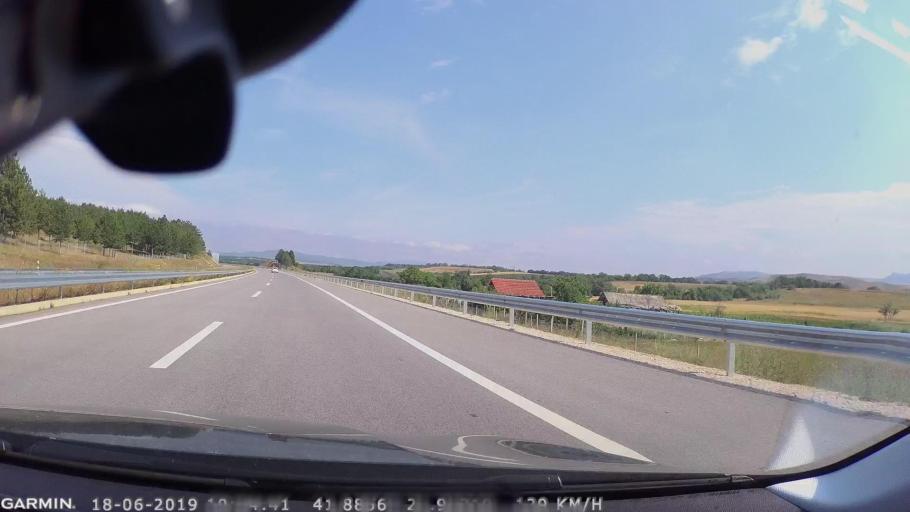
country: MK
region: Sveti Nikole
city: Sveti Nikole
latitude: 41.8867
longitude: 21.9324
